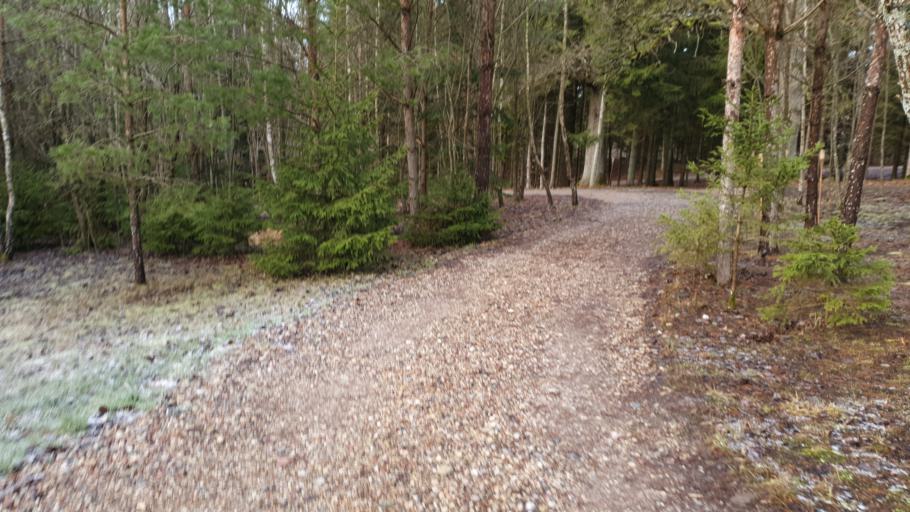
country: LT
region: Vilnius County
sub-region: Vilniaus Rajonas
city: Vievis
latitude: 54.8279
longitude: 24.9480
